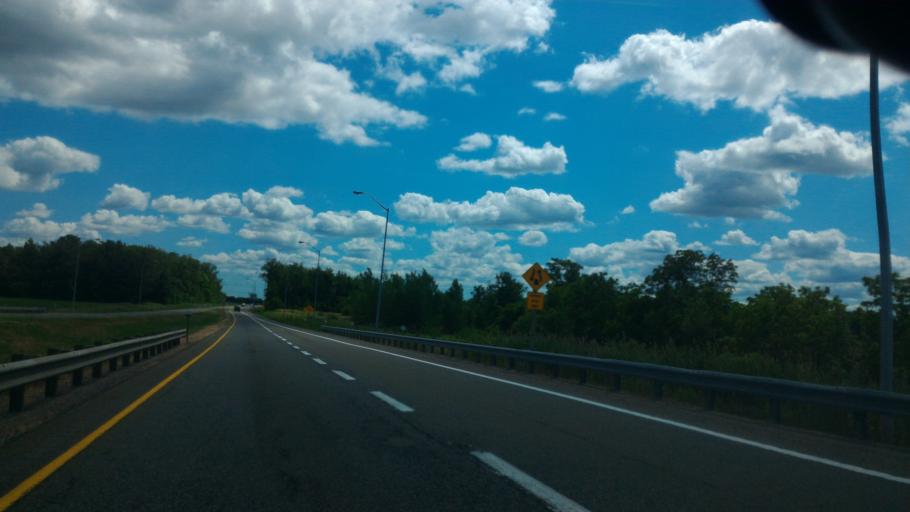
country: CA
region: Ontario
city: Ancaster
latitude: 43.2016
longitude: -79.9661
